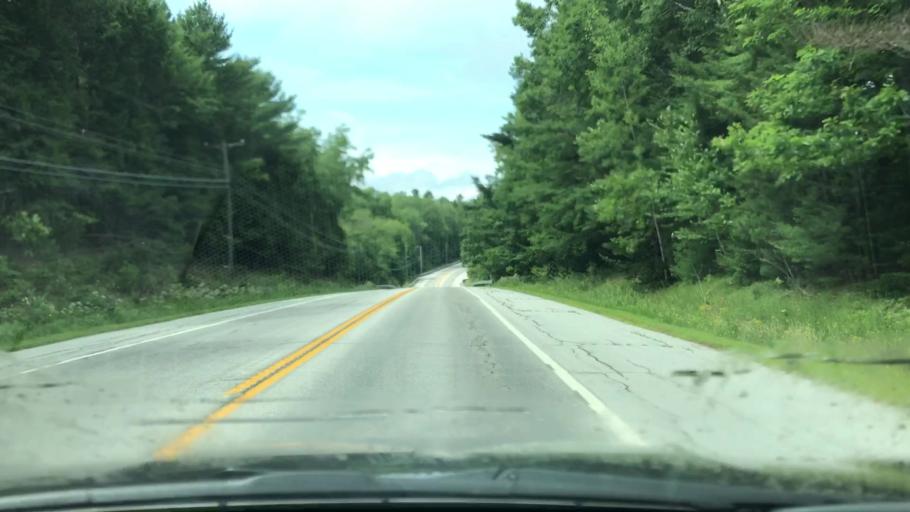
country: US
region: Maine
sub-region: Waldo County
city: Northport
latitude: 44.3407
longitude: -68.9661
